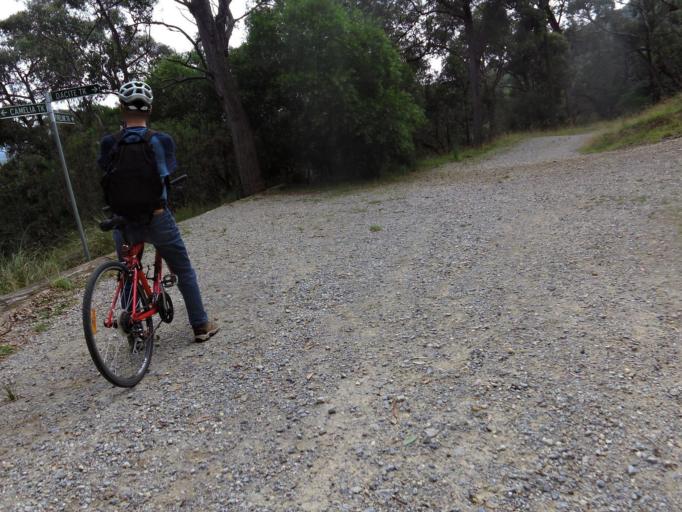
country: AU
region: Victoria
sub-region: Yarra Ranges
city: Montrose
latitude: -37.8317
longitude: 145.3422
